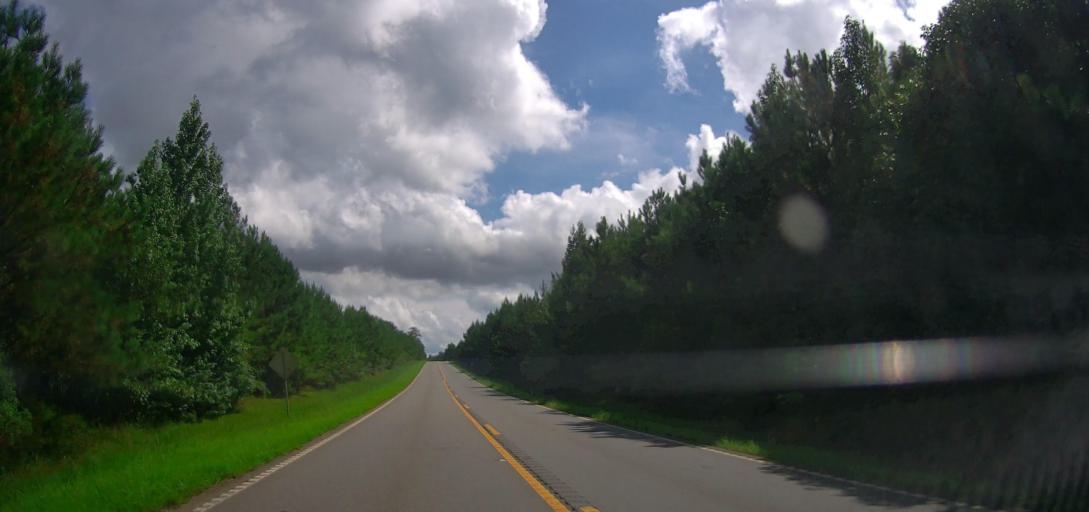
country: US
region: Georgia
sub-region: Talbot County
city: Talbotton
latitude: 32.6532
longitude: -84.5070
